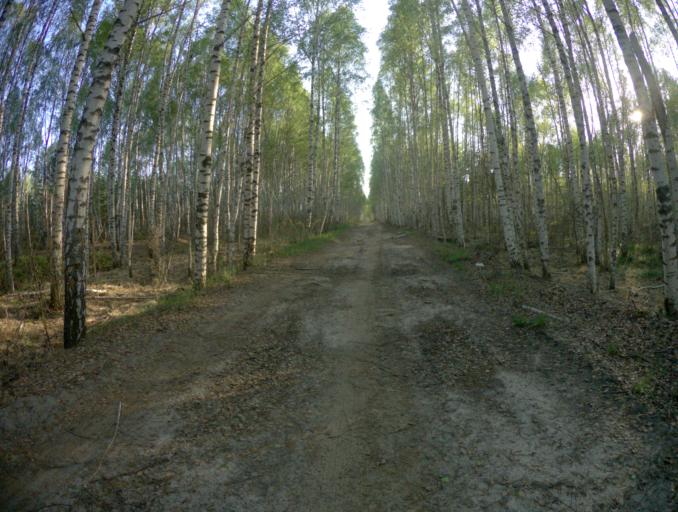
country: RU
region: Vladimir
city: Vyazniki
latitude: 56.3730
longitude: 42.1668
